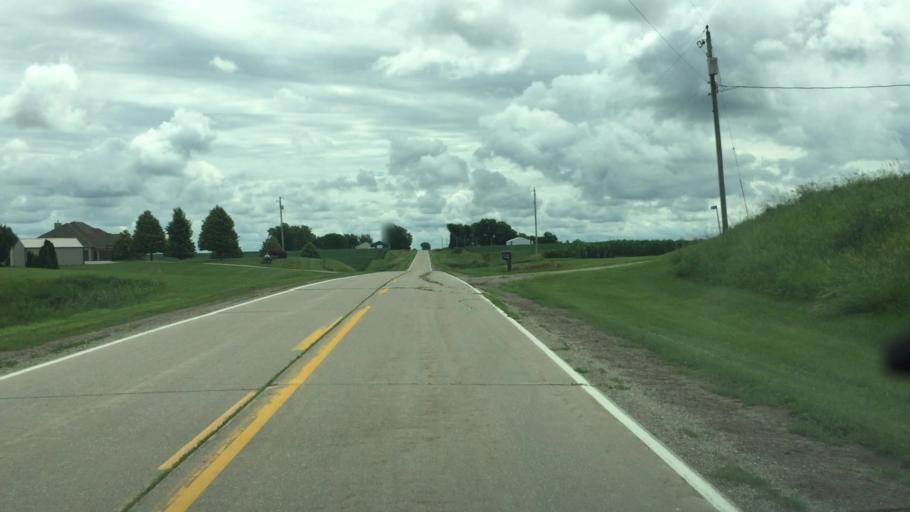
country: US
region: Iowa
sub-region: Jasper County
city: Monroe
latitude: 41.5807
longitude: -93.1197
